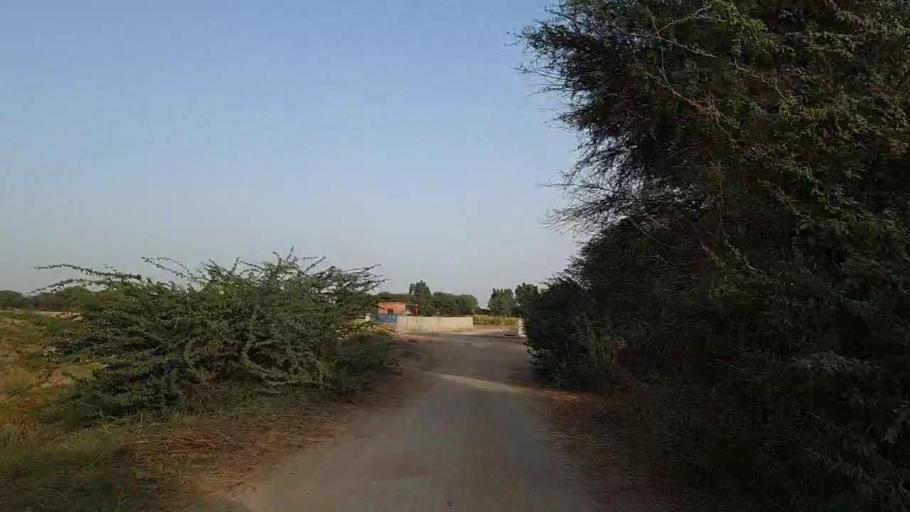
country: PK
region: Sindh
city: Jati
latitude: 24.4156
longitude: 68.1865
